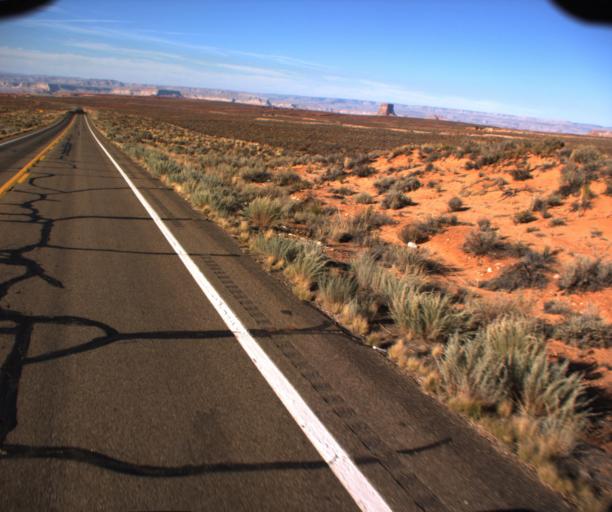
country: US
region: Arizona
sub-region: Coconino County
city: LeChee
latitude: 36.8648
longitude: -111.3397
